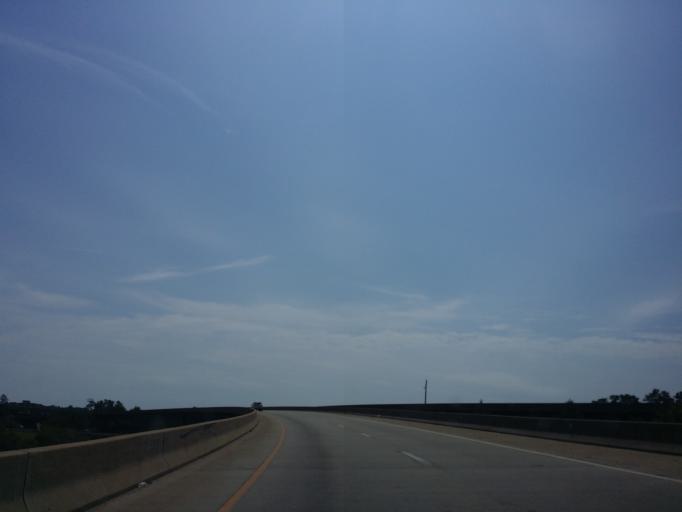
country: US
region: North Carolina
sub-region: Wake County
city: Morrisville
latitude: 35.9060
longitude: -78.7734
